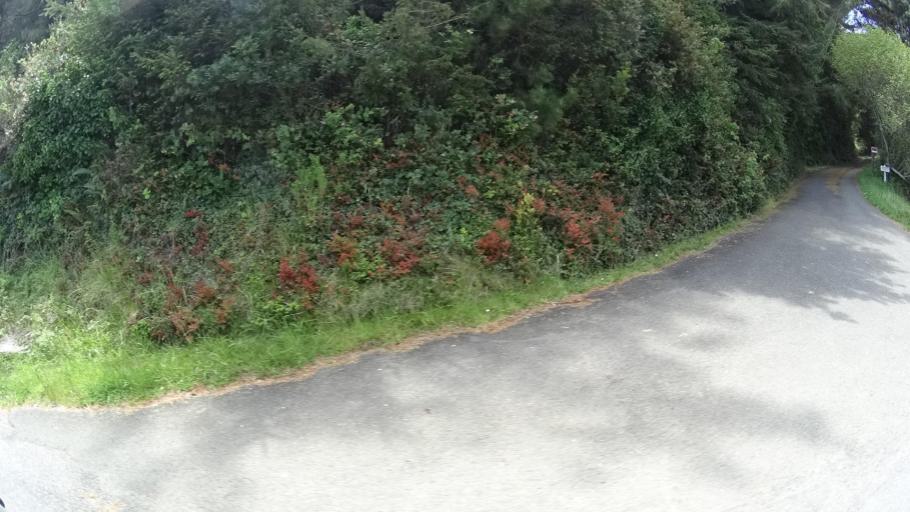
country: US
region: California
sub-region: Humboldt County
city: Humboldt Hill
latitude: 40.6790
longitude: -124.2288
